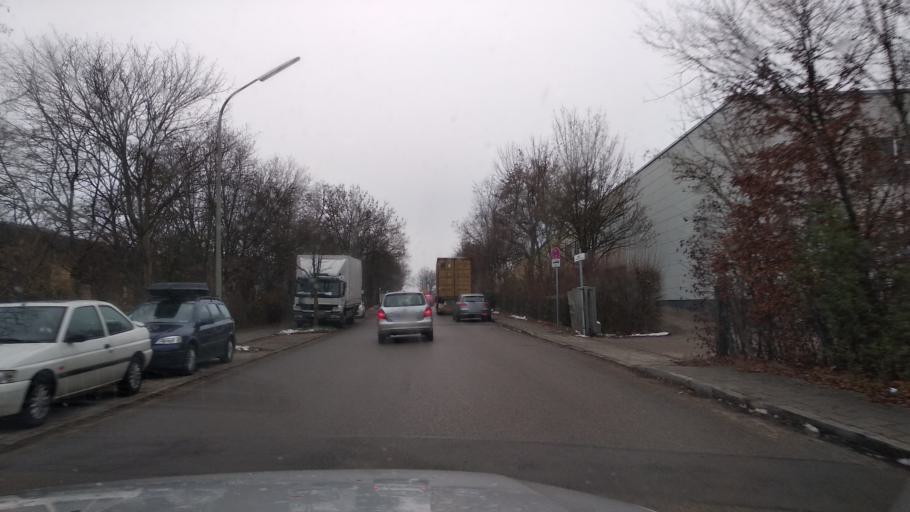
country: DE
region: Bavaria
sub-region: Upper Bavaria
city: Kirchheim bei Muenchen
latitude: 48.1547
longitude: 11.7531
